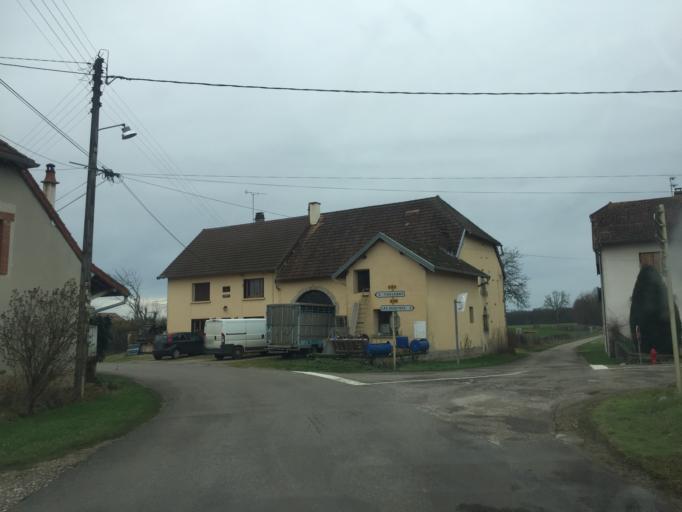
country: FR
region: Franche-Comte
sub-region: Departement du Jura
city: Mont-sous-Vaudrey
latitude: 46.8721
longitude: 5.5229
